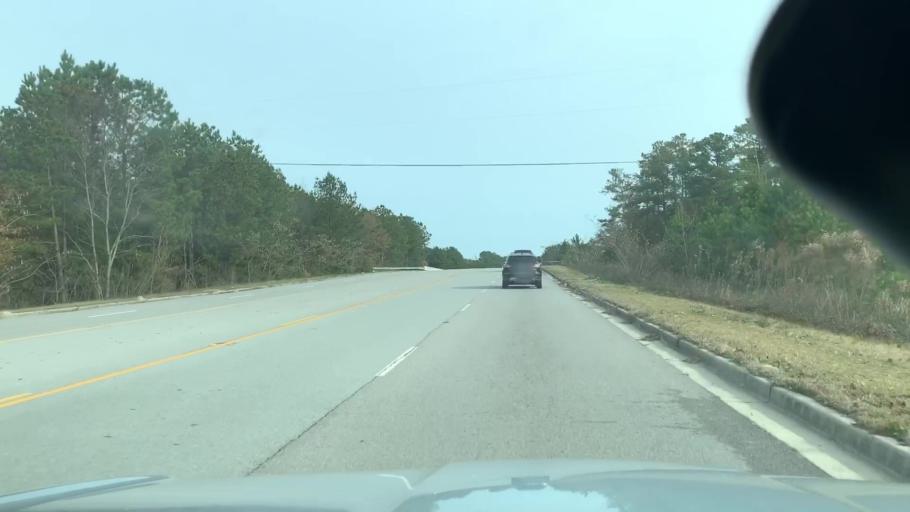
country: US
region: South Carolina
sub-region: Richland County
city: Woodfield
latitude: 34.0785
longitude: -80.9386
